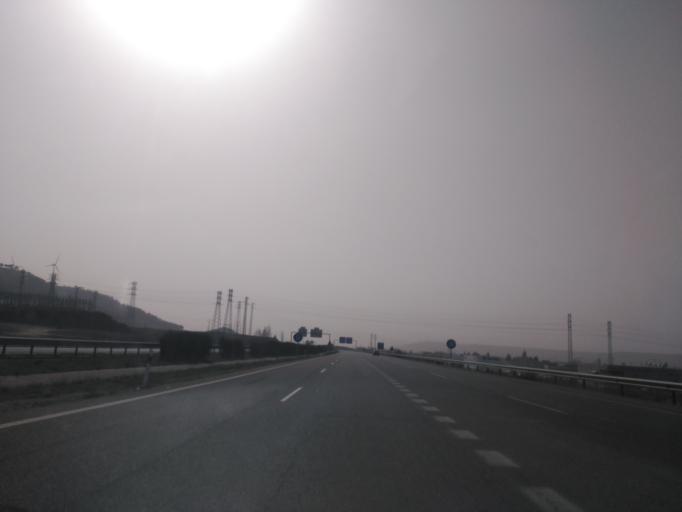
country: ES
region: Castille and Leon
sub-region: Provincia de Palencia
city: Palencia
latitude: 42.0017
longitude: -4.5018
